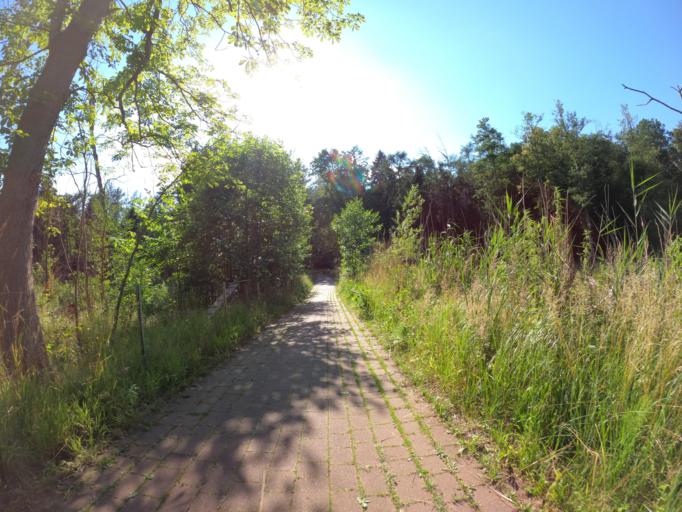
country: DE
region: Brandenburg
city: Mescherin
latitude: 53.2360
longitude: 14.4149
